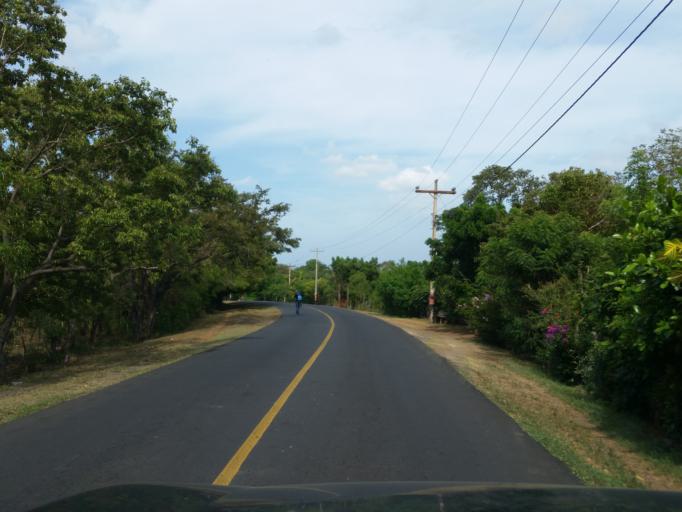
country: NI
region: Managua
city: San Rafael del Sur
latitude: 11.8977
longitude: -86.3978
